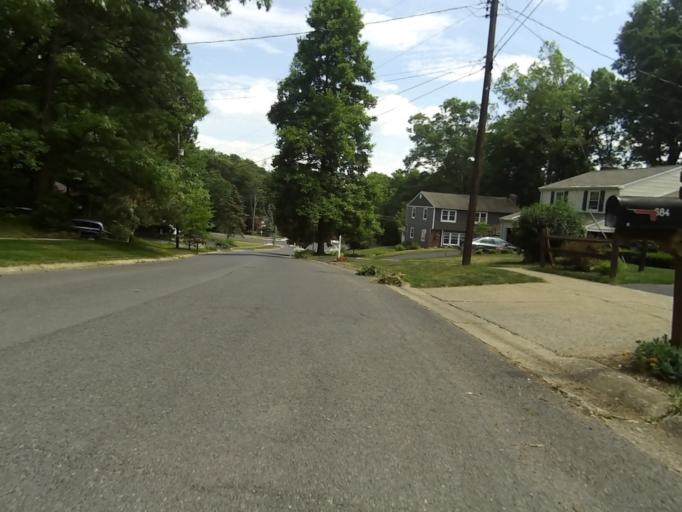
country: US
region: Pennsylvania
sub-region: Centre County
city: Park Forest Village
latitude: 40.8003
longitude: -77.9063
